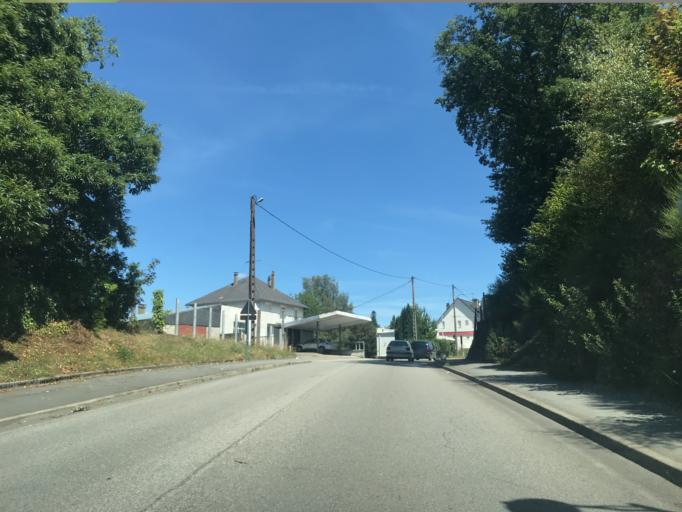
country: FR
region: Limousin
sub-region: Departement de la Correze
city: Egletons
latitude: 45.4012
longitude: 2.0395
